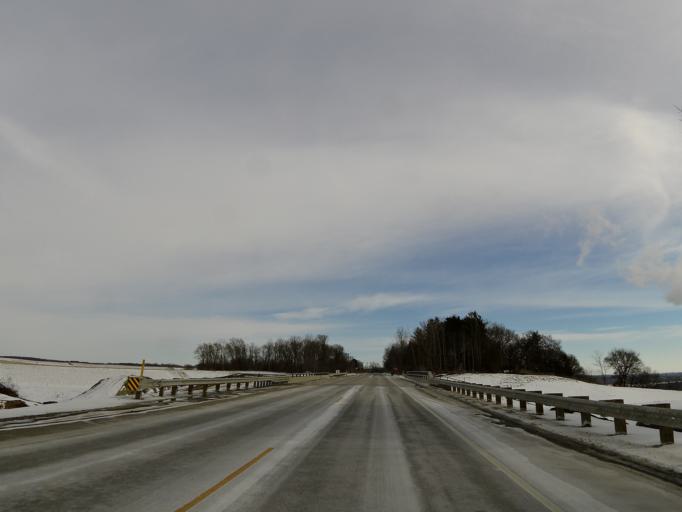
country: US
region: Minnesota
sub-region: Washington County
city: Oak Park Heights
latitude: 45.0476
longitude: -92.7812
